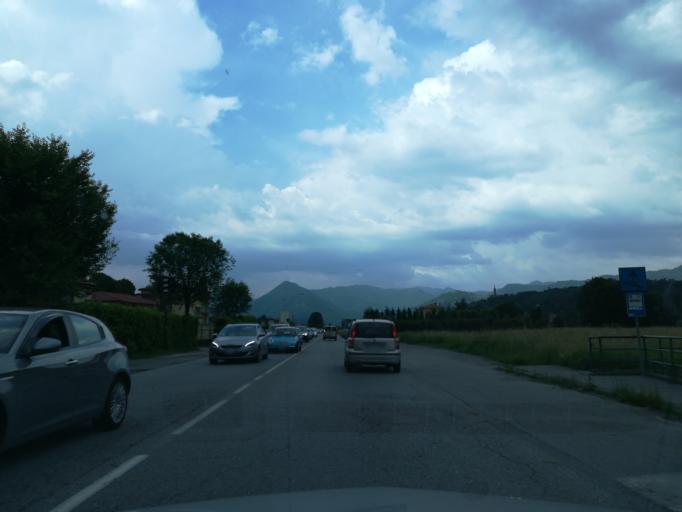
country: IT
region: Lombardy
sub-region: Provincia di Bergamo
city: Scano al Brembo
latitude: 45.7201
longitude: 9.6102
